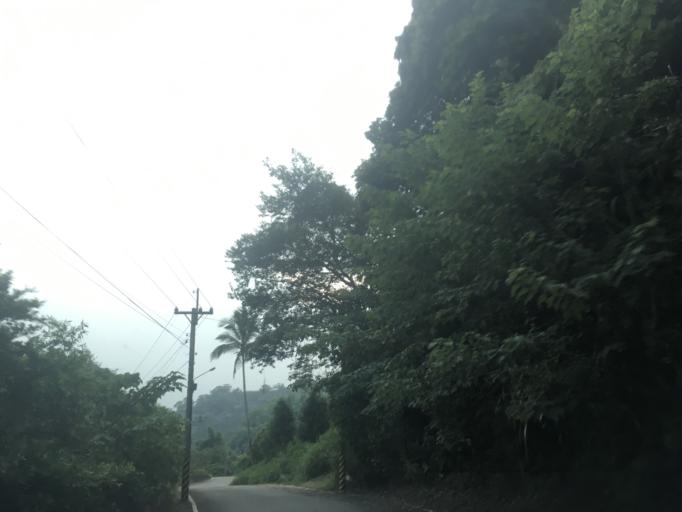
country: TW
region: Taiwan
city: Fengyuan
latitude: 24.1904
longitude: 120.7749
